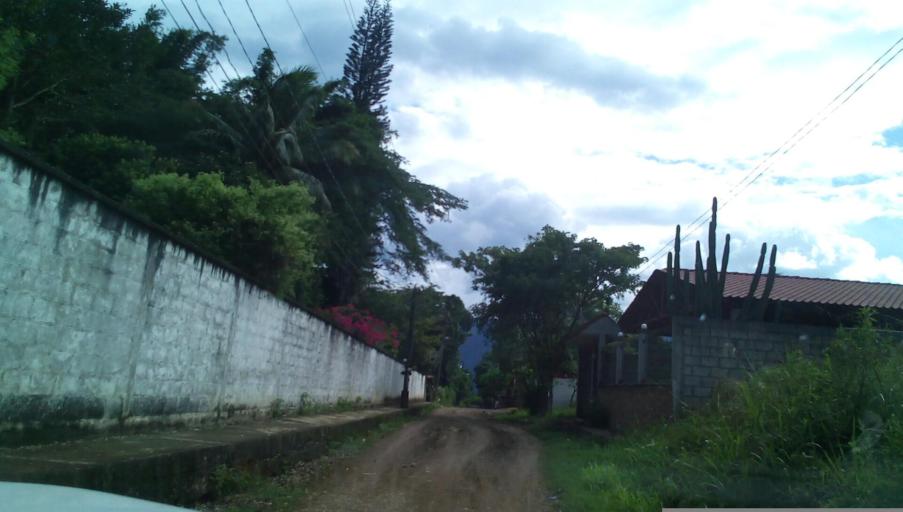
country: MX
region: Veracruz
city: Amatlan de los Reyes
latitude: 18.8253
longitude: -96.9216
